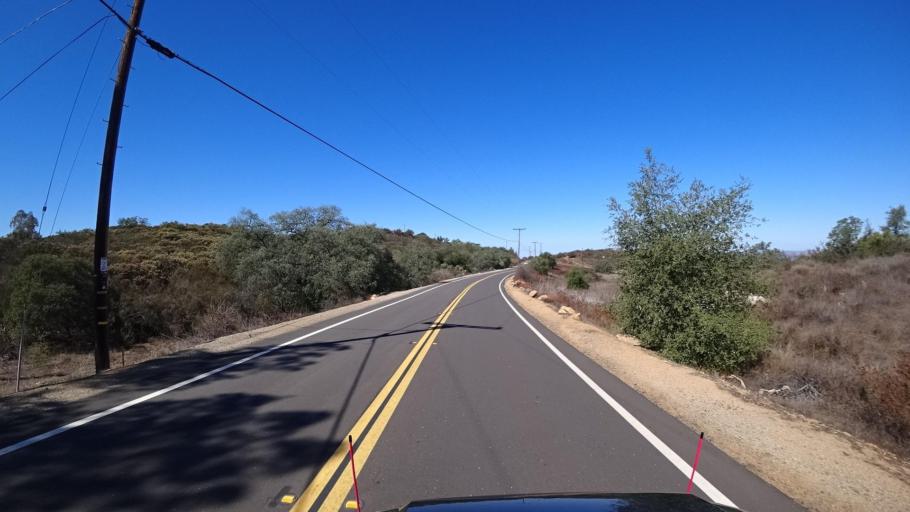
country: US
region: California
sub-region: San Diego County
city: Jamul
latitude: 32.7265
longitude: -116.7752
